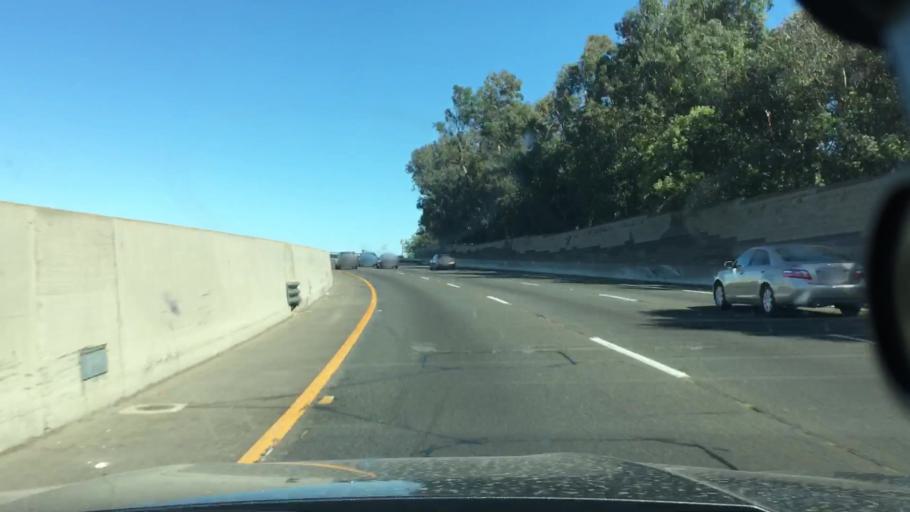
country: US
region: California
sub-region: Sacramento County
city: Sacramento
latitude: 38.5859
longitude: -121.4491
